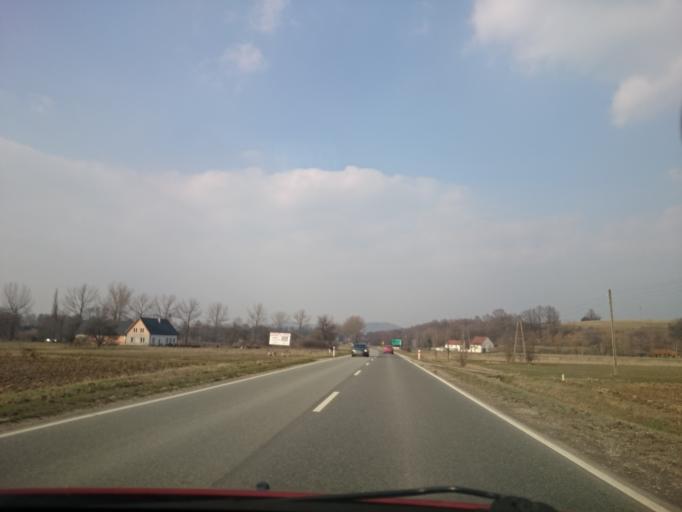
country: PL
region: Lower Silesian Voivodeship
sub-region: Powiat klodzki
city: Bystrzyca Klodzka
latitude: 50.3125
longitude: 16.6606
